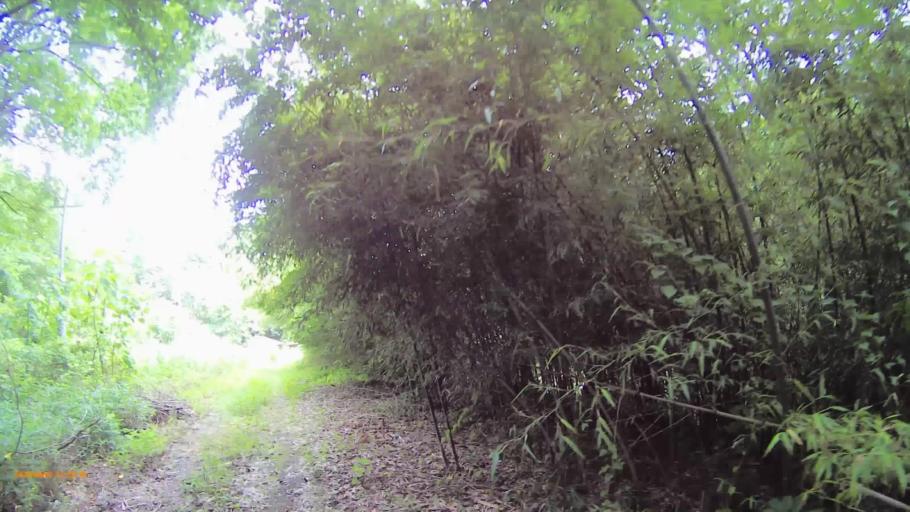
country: JP
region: Nagano
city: Shiojiri
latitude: 36.0198
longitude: 137.8644
